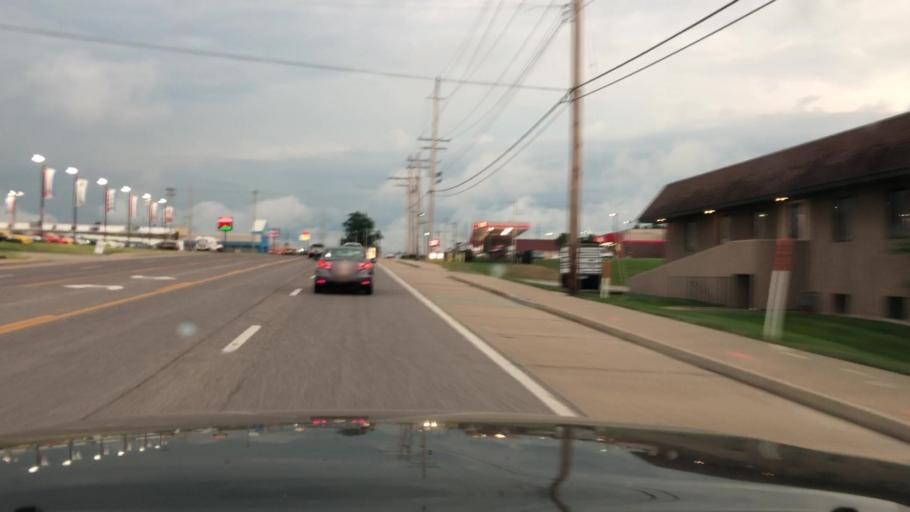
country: US
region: Missouri
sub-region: Saint Louis County
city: Bridgeton
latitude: 38.7421
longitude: -90.4077
